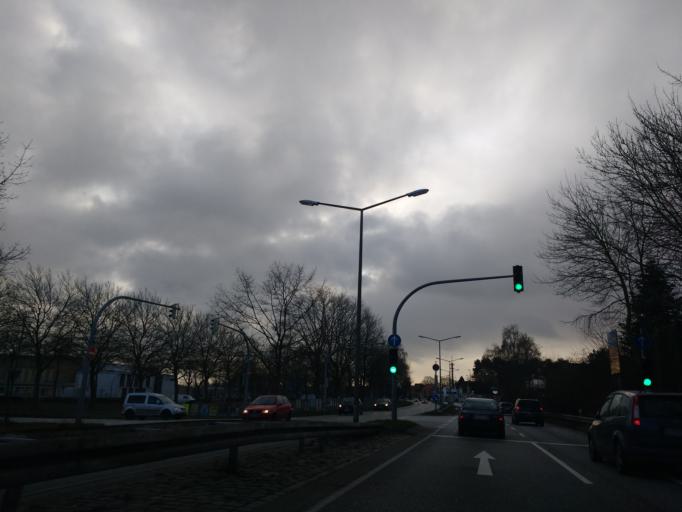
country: DE
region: Schleswig-Holstein
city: Neumunster
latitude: 54.0947
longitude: 9.9739
